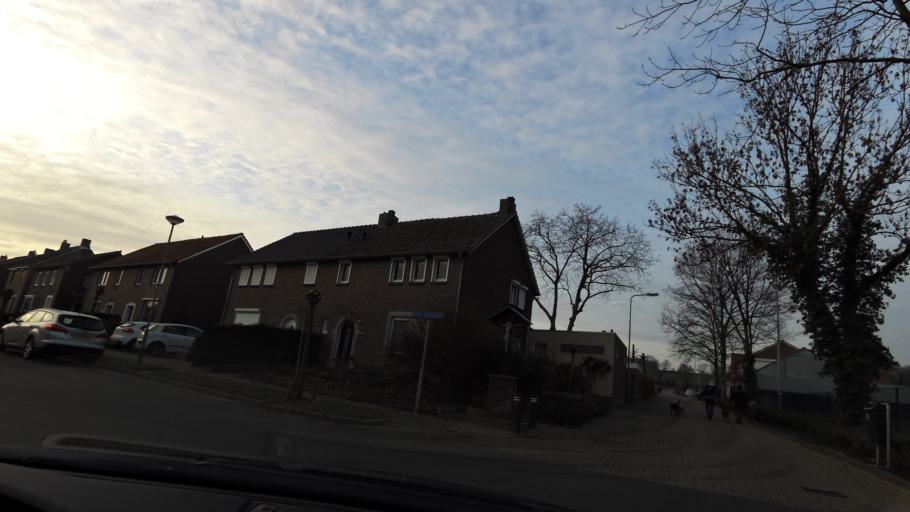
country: NL
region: Limburg
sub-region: Gemeente Schinnen
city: Puth
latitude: 50.9373
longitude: 5.8386
